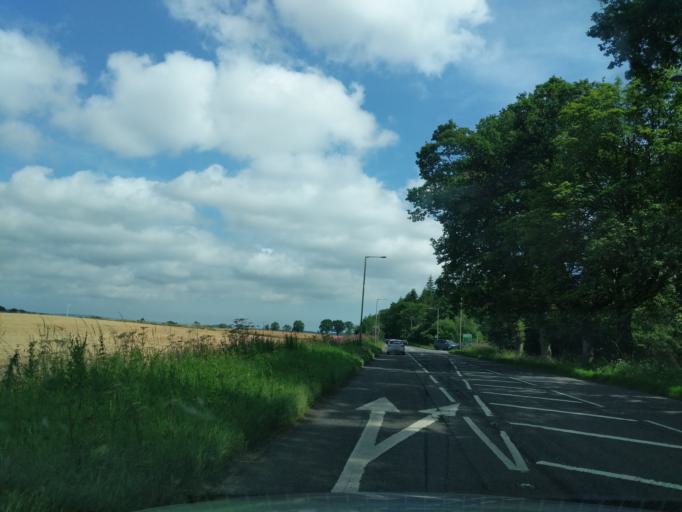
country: GB
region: Scotland
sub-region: Angus
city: Muirhead
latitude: 56.5050
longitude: -3.1331
